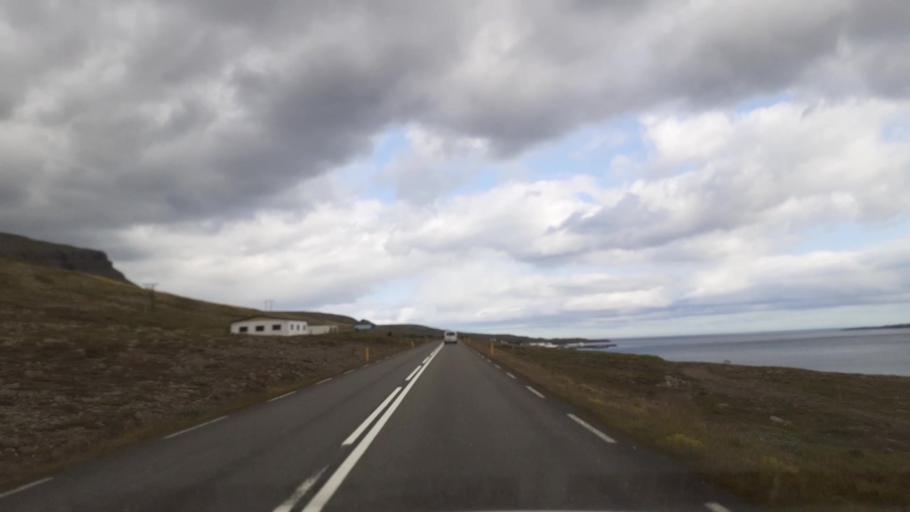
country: IS
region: East
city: Eskifjoerdur
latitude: 64.8395
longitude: -13.9165
